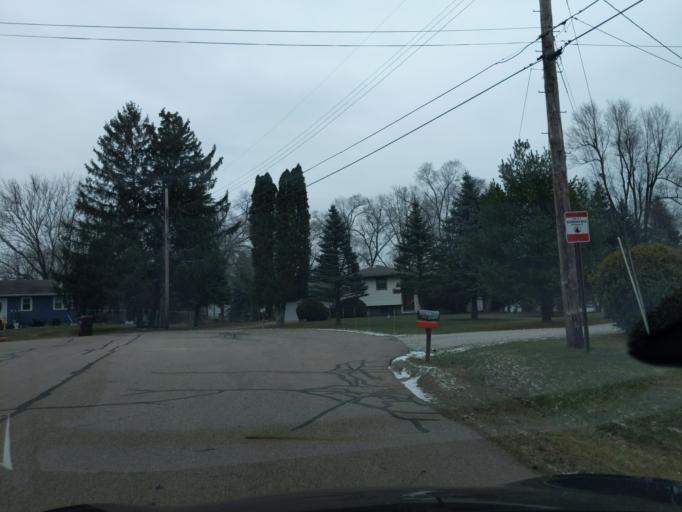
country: US
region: Michigan
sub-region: Eaton County
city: Waverly
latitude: 42.7035
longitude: -84.6196
